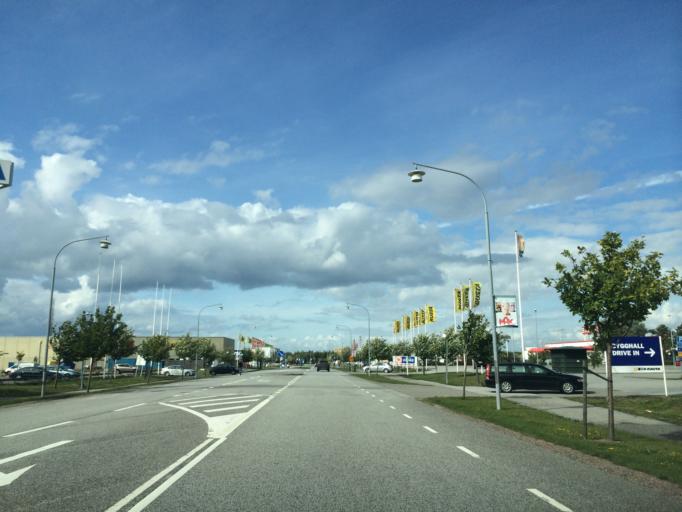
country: SE
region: Skane
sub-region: Malmo
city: Tygelsjo
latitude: 55.5496
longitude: 12.9952
